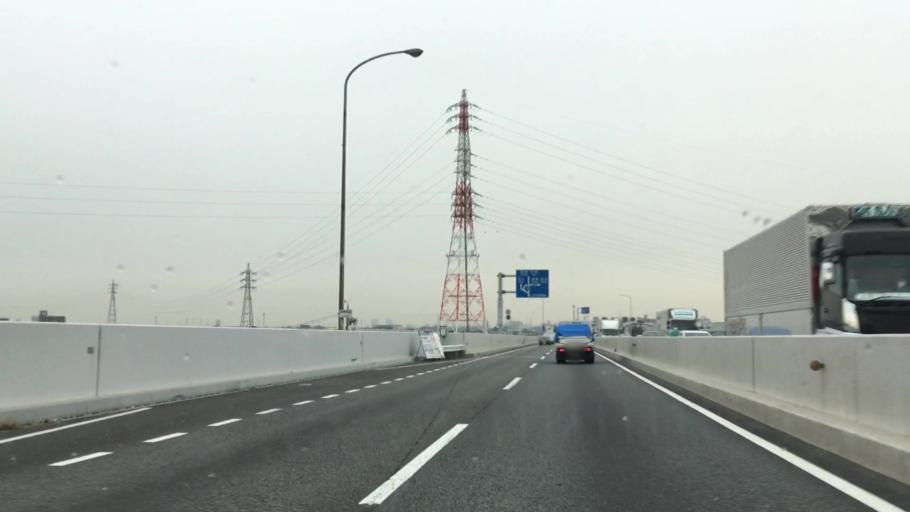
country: JP
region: Aichi
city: Chiryu
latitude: 34.9957
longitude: 137.0329
